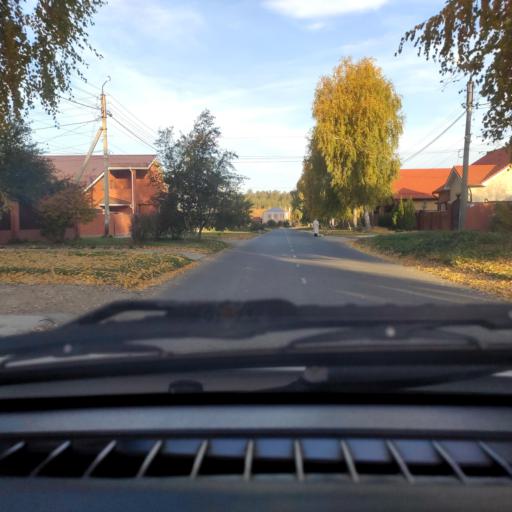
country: RU
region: Samara
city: Tol'yatti
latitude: 53.5181
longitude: 49.3980
